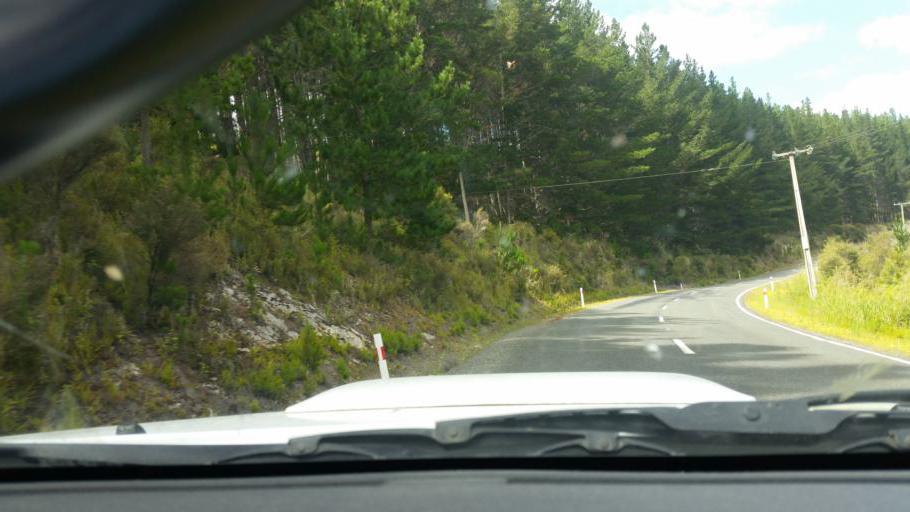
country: NZ
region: Northland
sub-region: Kaipara District
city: Dargaville
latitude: -35.8204
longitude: 173.7106
